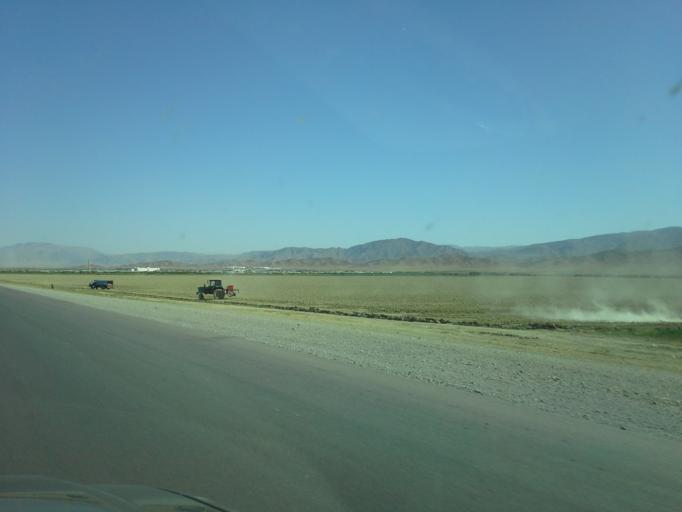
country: TM
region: Ahal
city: Baharly
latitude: 38.3943
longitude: 57.4808
